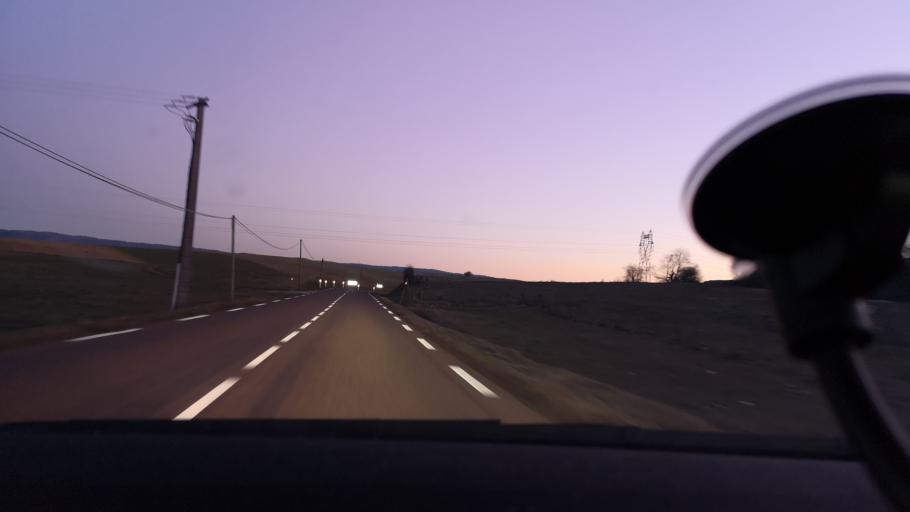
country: FR
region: Franche-Comte
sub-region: Departement du Jura
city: Champagnole
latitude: 46.7889
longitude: 6.0086
